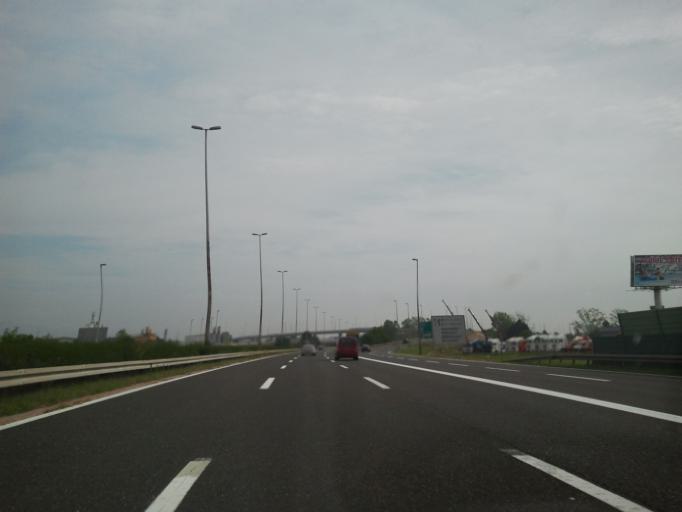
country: HR
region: Grad Zagreb
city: Lucko
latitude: 45.7541
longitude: 15.8902
